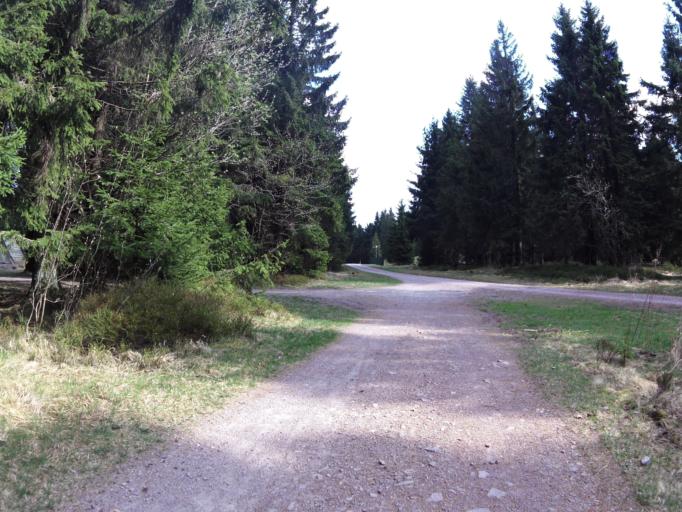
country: DE
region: Thuringia
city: Oberhof
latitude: 50.7018
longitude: 10.7058
